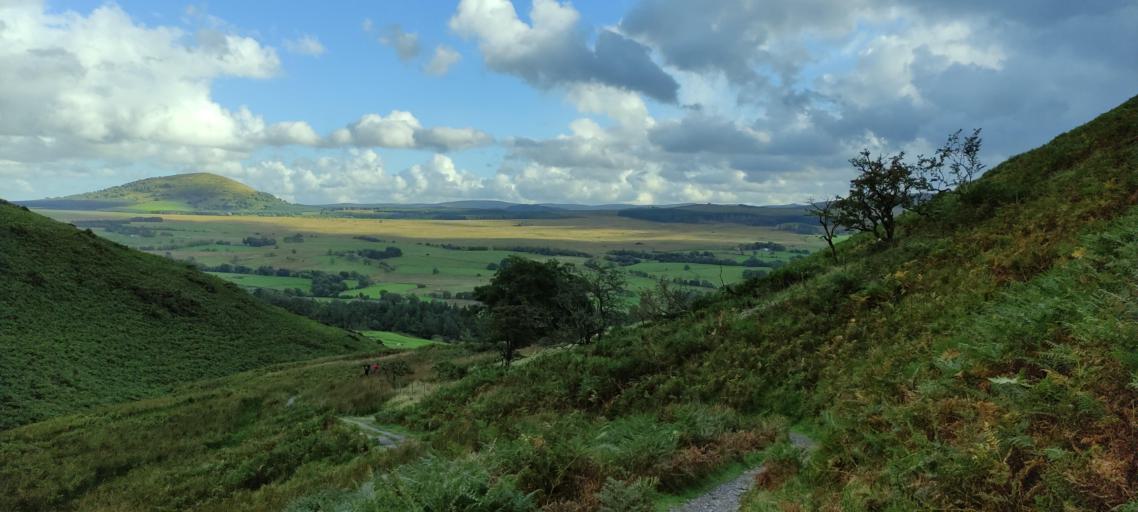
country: GB
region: England
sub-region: Cumbria
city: Keswick
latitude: 54.6376
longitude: -3.0138
